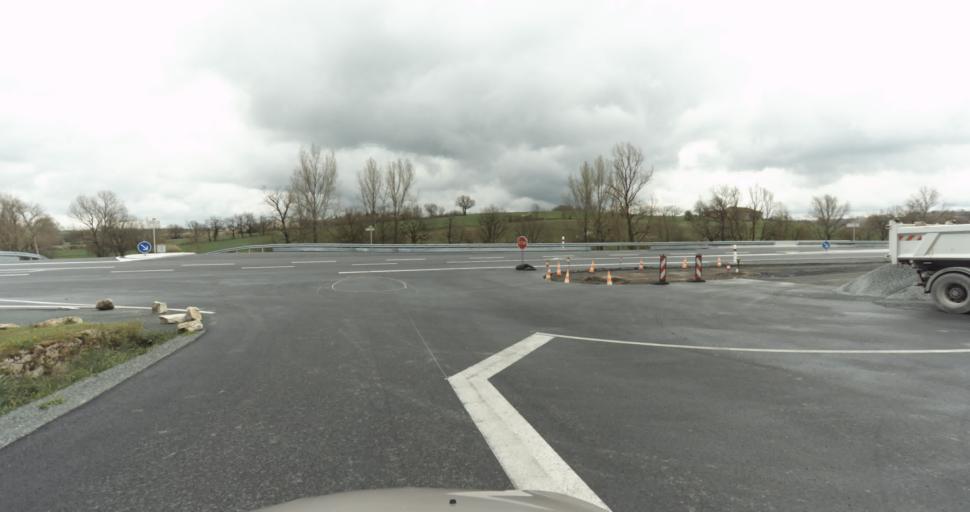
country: FR
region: Midi-Pyrenees
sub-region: Departement du Tarn
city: Puygouzon
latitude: 43.8570
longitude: 2.1887
